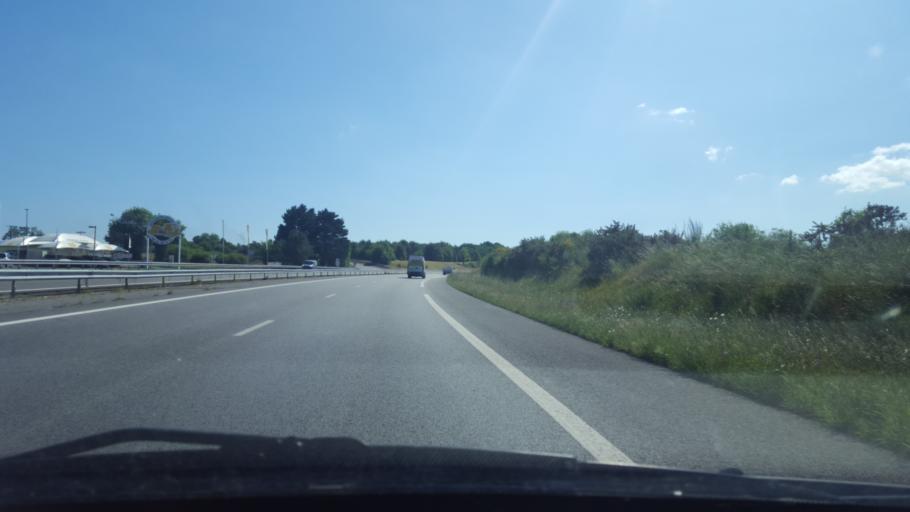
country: FR
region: Pays de la Loire
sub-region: Departement de la Loire-Atlantique
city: Saint-Philbert-de-Grand-Lieu
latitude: 47.0360
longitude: -1.6545
